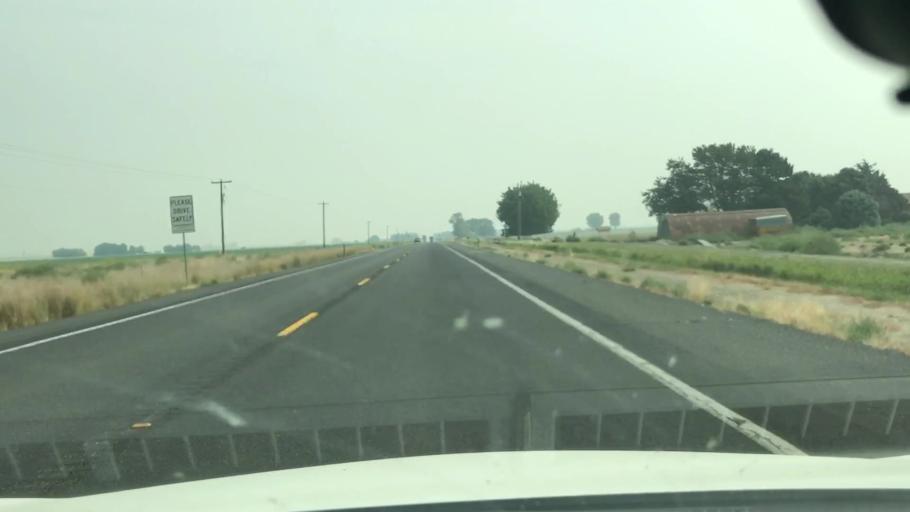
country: US
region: Washington
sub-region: Grant County
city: Quincy
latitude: 47.2341
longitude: -119.7802
